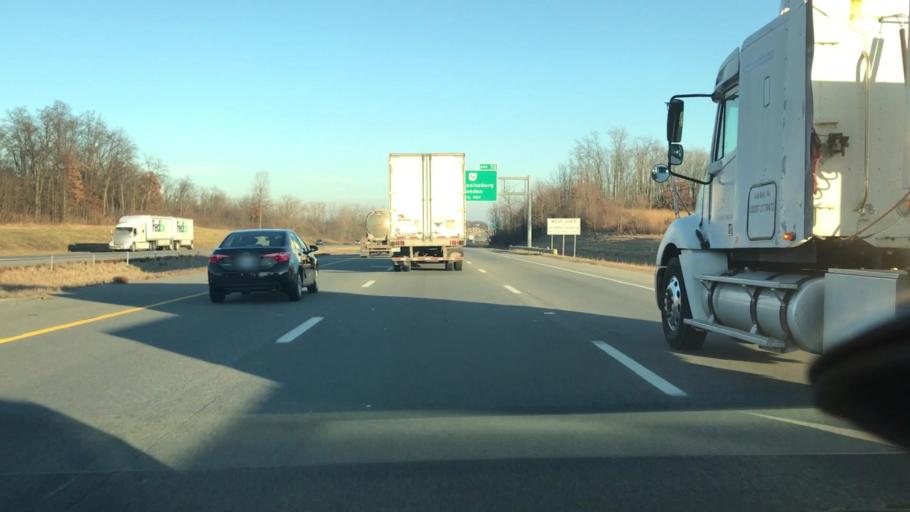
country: US
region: Ohio
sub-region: Madison County
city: Choctaw Lake
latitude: 39.9420
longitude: -83.5137
